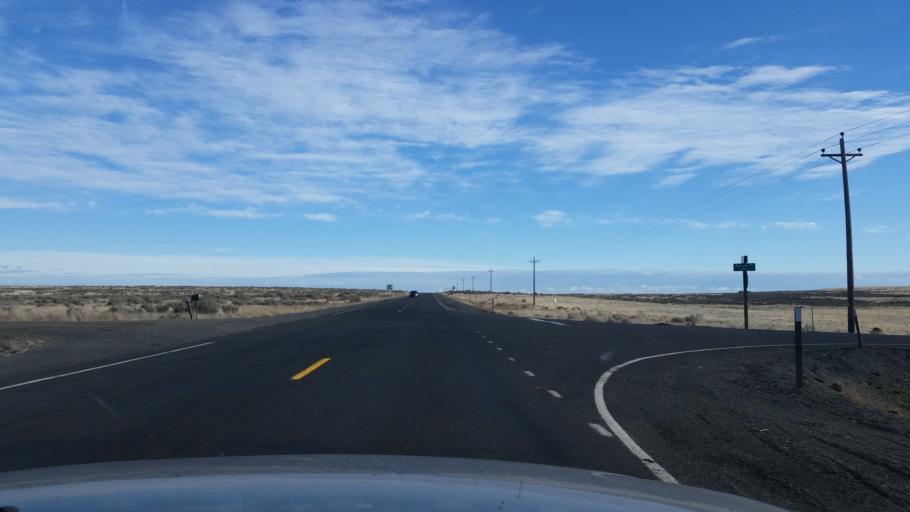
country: US
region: Washington
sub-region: Grant County
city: Warden
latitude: 47.3155
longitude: -118.8091
